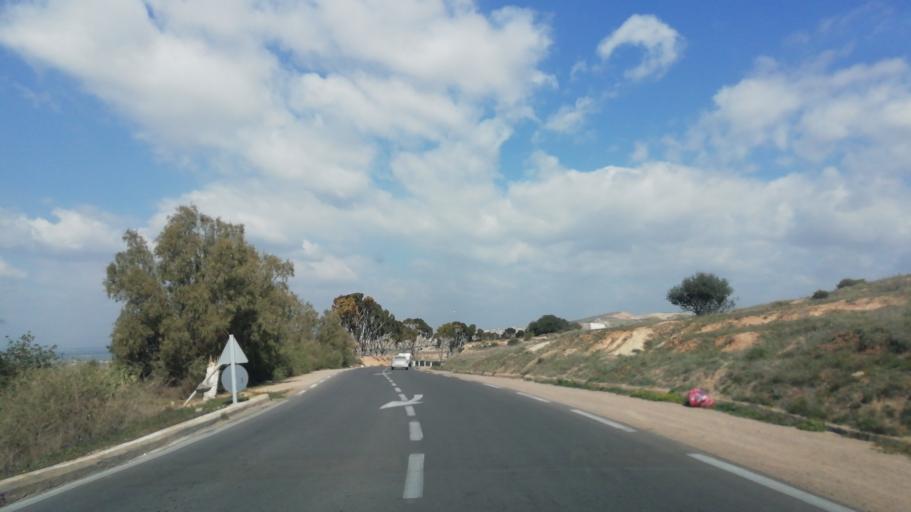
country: DZ
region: Mascara
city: Mascara
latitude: 35.5451
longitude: 0.0819
